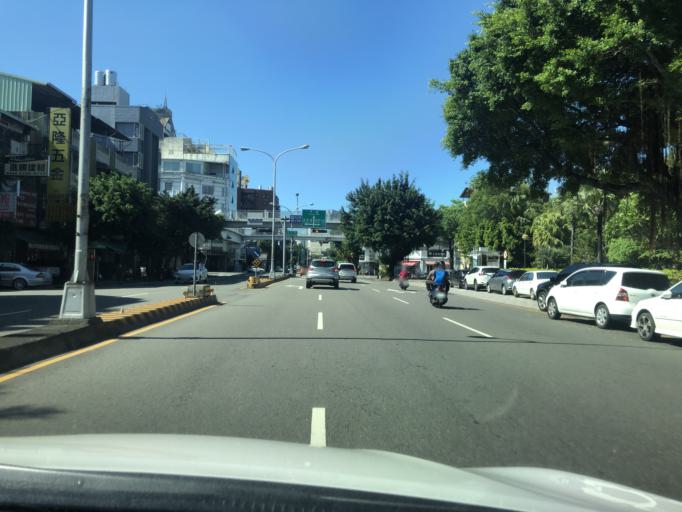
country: TW
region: Taiwan
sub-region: Taichung City
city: Taichung
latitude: 24.1601
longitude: 120.6850
